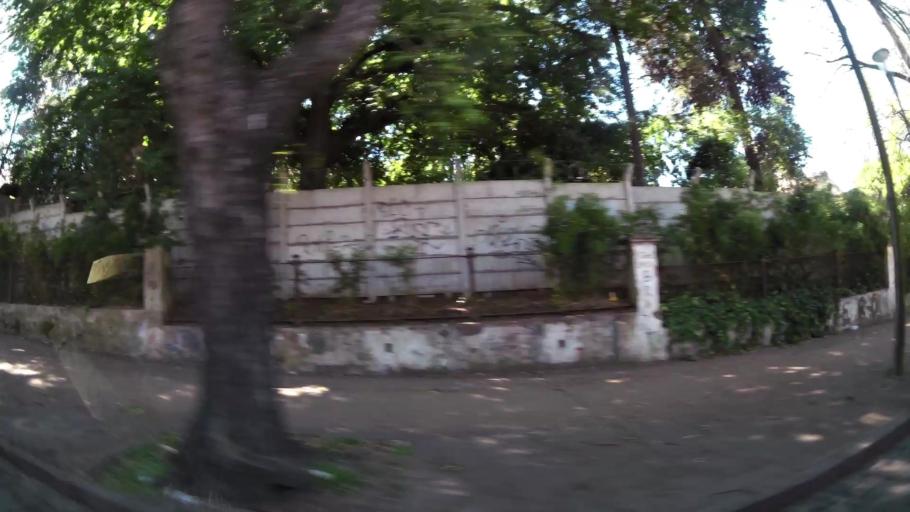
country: AR
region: Buenos Aires
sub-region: Partido de San Isidro
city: San Isidro
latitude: -34.4653
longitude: -58.5114
